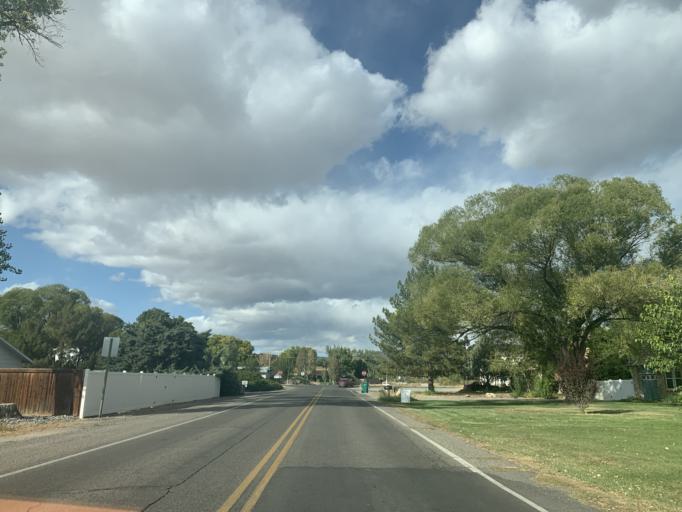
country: US
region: Colorado
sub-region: Mesa County
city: Fruitvale
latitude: 39.0836
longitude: -108.4785
